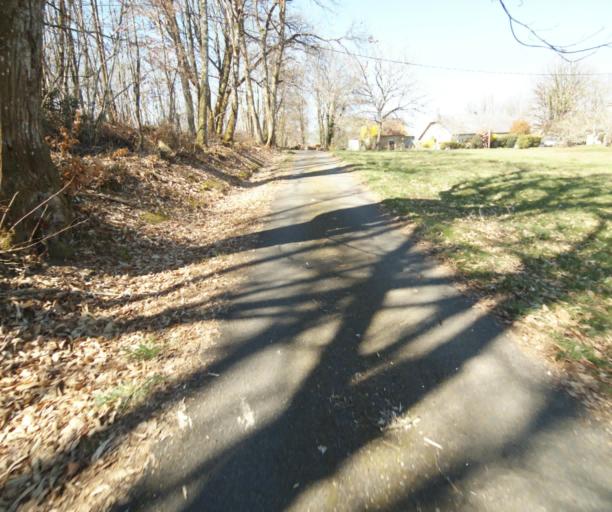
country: FR
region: Limousin
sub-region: Departement de la Correze
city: Saint-Mexant
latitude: 45.2970
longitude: 1.6408
